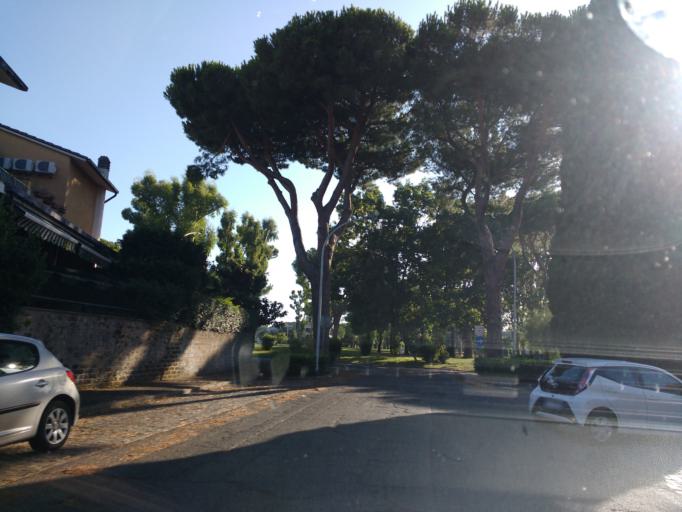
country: IT
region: Latium
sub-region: Citta metropolitana di Roma Capitale
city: Acilia-Castel Fusano-Ostia Antica
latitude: 41.7560
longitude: 12.3622
